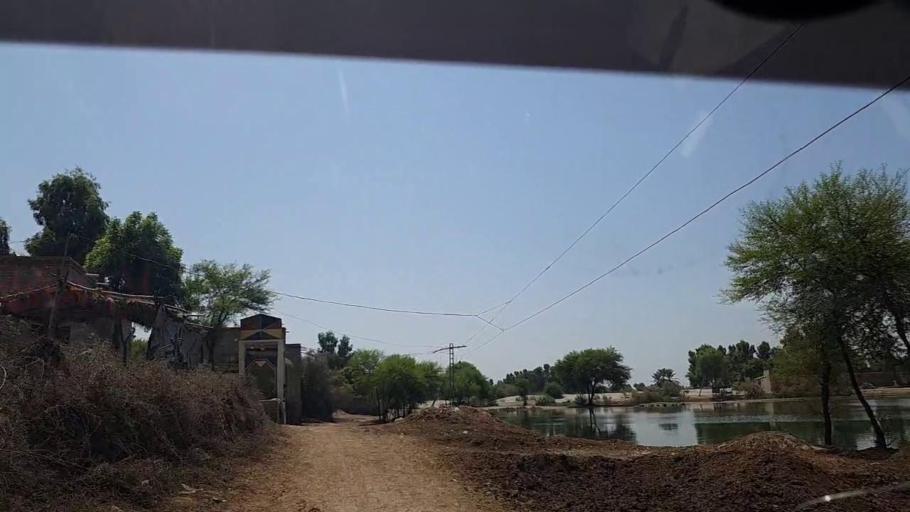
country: PK
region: Sindh
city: Ghauspur
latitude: 28.1592
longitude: 69.1238
